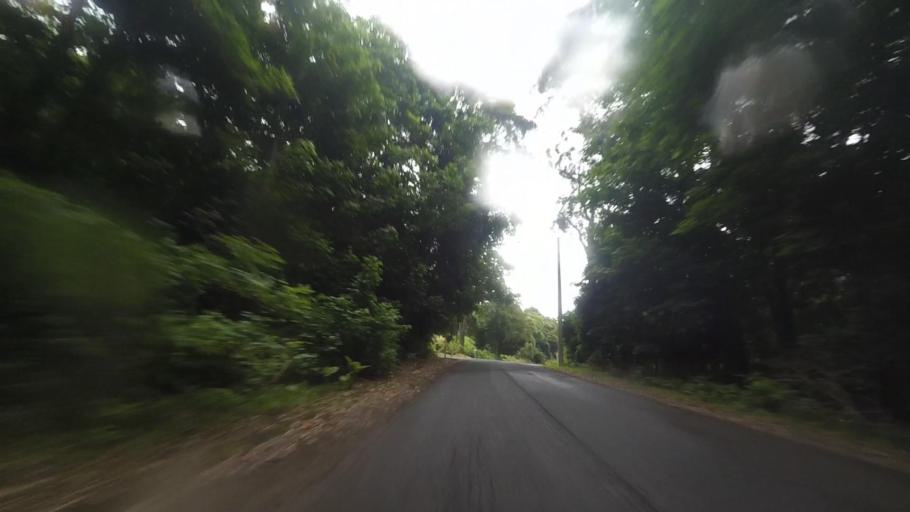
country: AU
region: New South Wales
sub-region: Wollongong
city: Cordeaux Heights
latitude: -34.4259
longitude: 150.8110
